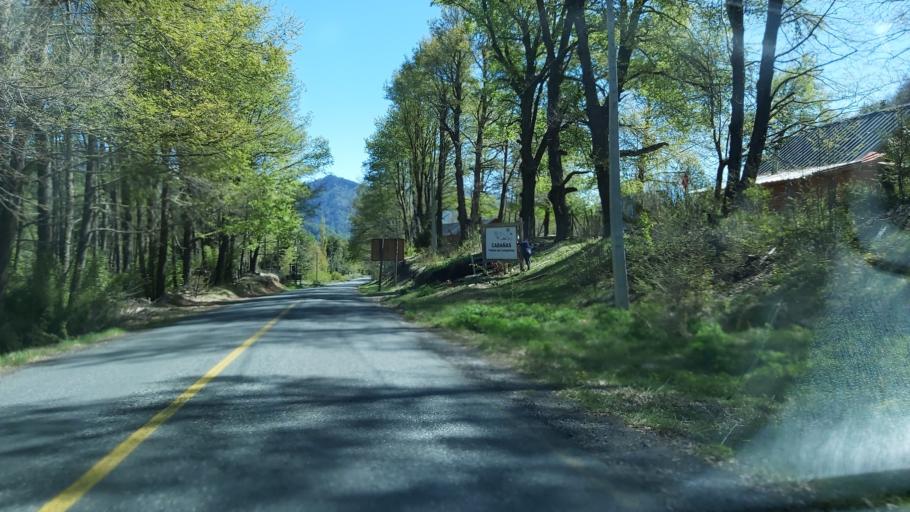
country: CL
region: Araucania
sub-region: Provincia de Cautin
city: Vilcun
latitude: -38.4669
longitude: -71.5204
